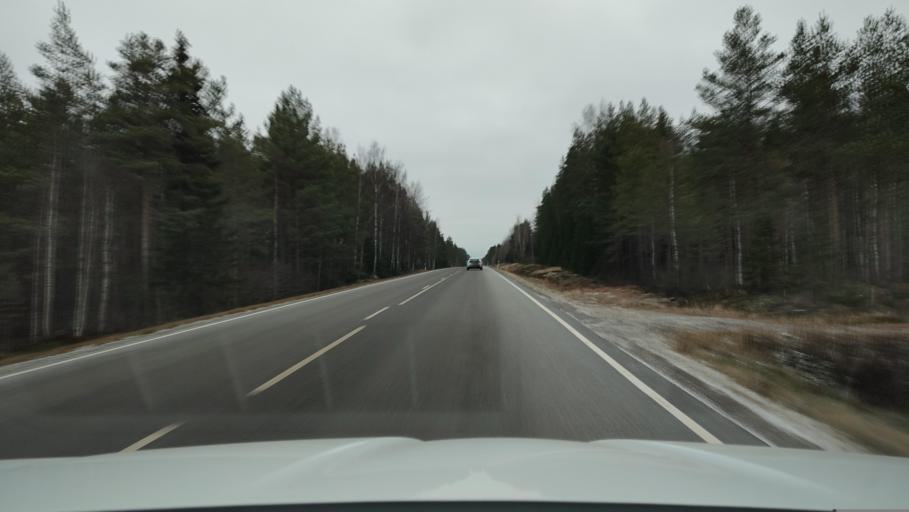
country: FI
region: Ostrobothnia
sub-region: Sydosterbotten
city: Naerpes
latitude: 62.5763
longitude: 21.4907
